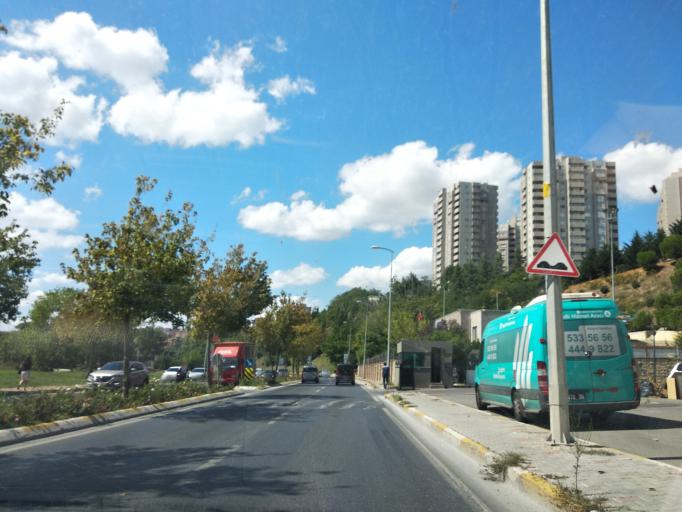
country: TR
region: Istanbul
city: Umraniye
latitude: 41.0062
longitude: 29.1113
